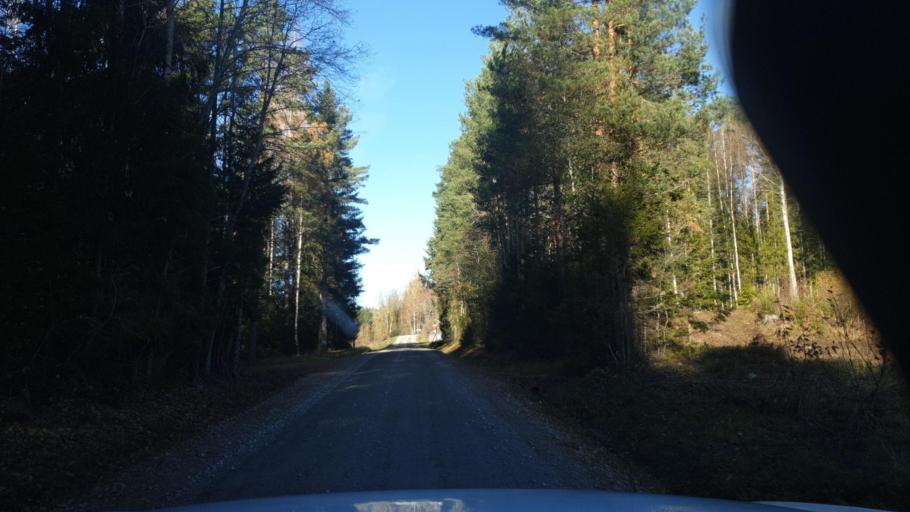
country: SE
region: Vaermland
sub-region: Karlstads Kommun
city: Edsvalla
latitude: 59.5324
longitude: 12.9960
